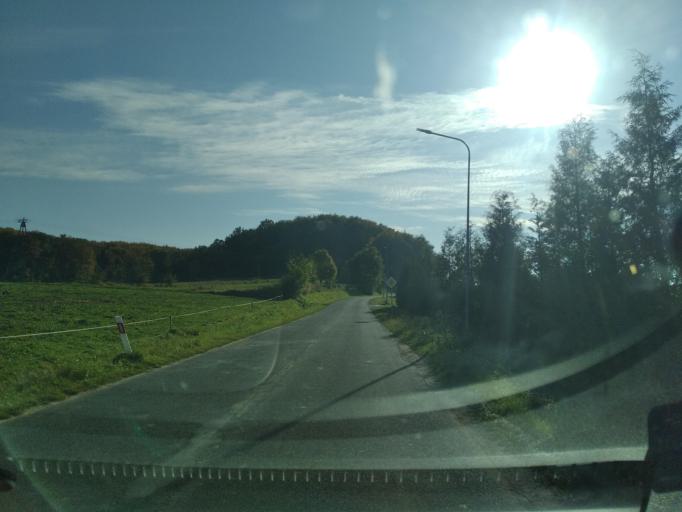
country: PL
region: Subcarpathian Voivodeship
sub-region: Powiat krosnienski
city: Sieniawa
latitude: 49.5729
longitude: 21.9429
